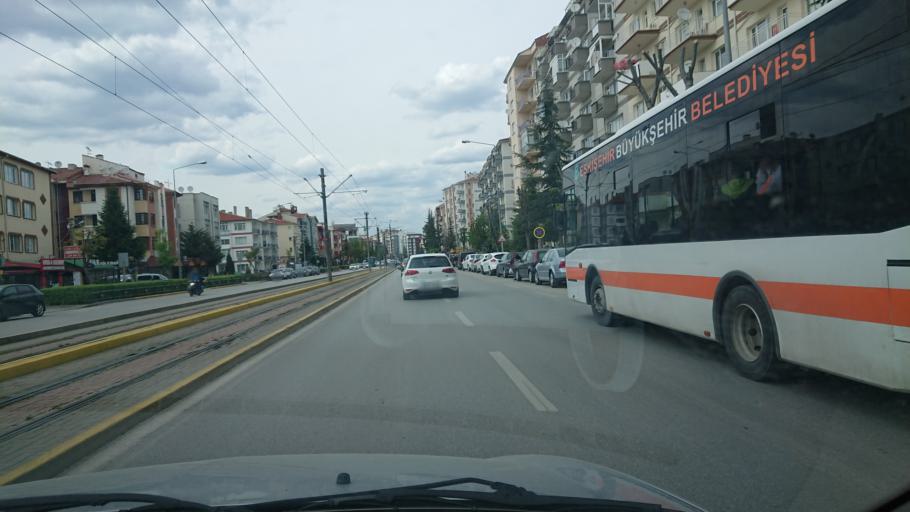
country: TR
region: Eskisehir
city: Eskisehir
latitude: 39.7660
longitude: 30.5006
